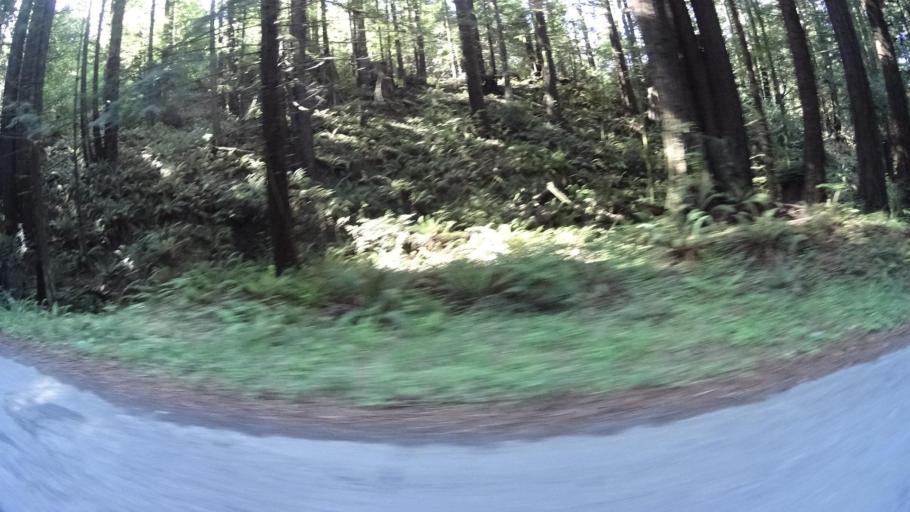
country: US
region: California
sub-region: Humboldt County
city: Rio Dell
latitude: 40.4539
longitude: -124.0288
